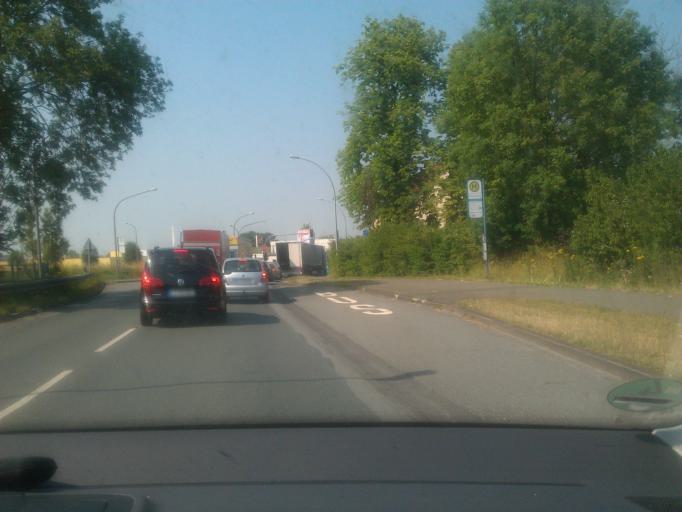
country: DE
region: North Rhine-Westphalia
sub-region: Regierungsbezirk Detmold
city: Oerlinghausen
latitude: 51.9743
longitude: 8.6656
